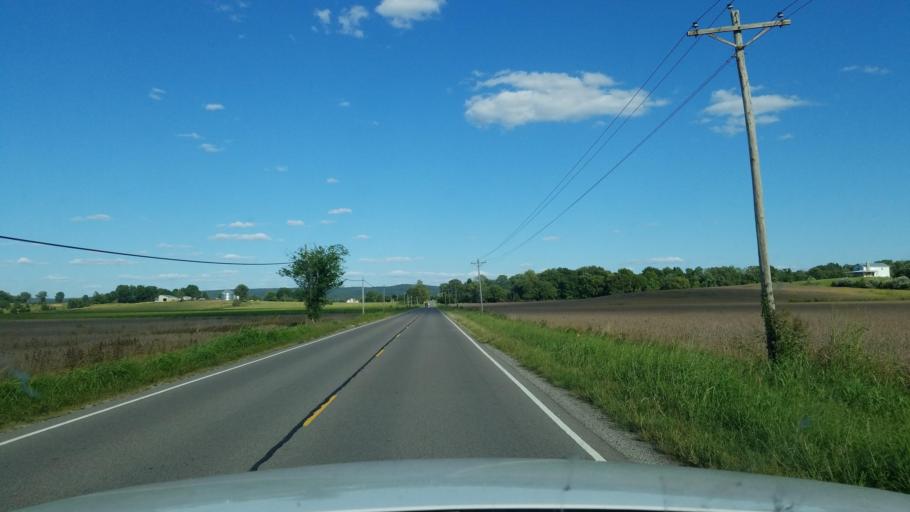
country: US
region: Illinois
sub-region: Saline County
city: Harrisburg
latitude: 37.6364
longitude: -88.5157
